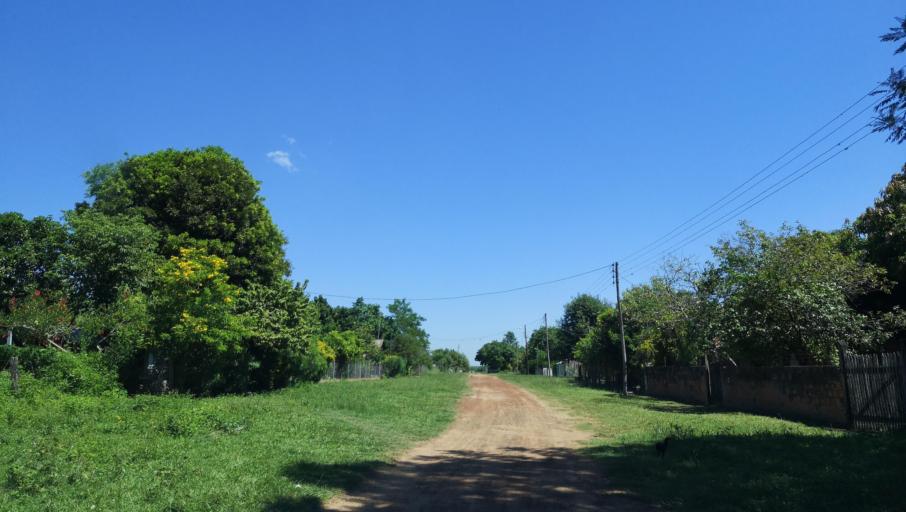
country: PY
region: Caaguazu
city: Carayao
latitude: -25.1927
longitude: -56.4006
